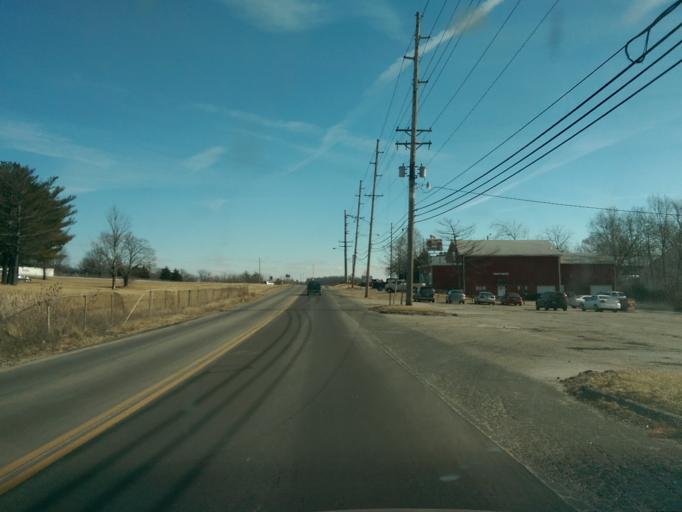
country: US
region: Missouri
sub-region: Boone County
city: Columbia
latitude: 38.9638
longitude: -92.3036
